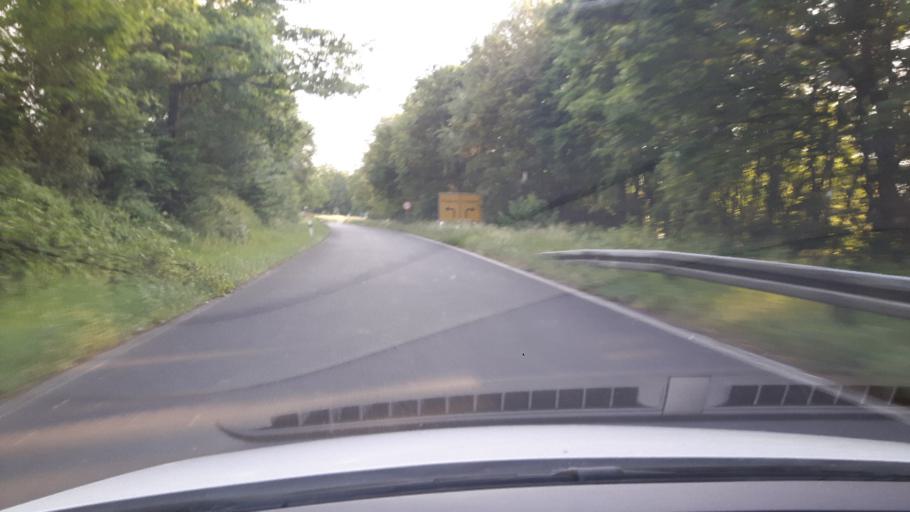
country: DE
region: North Rhine-Westphalia
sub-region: Regierungsbezirk Koln
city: Siegburg
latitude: 50.8124
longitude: 7.1896
